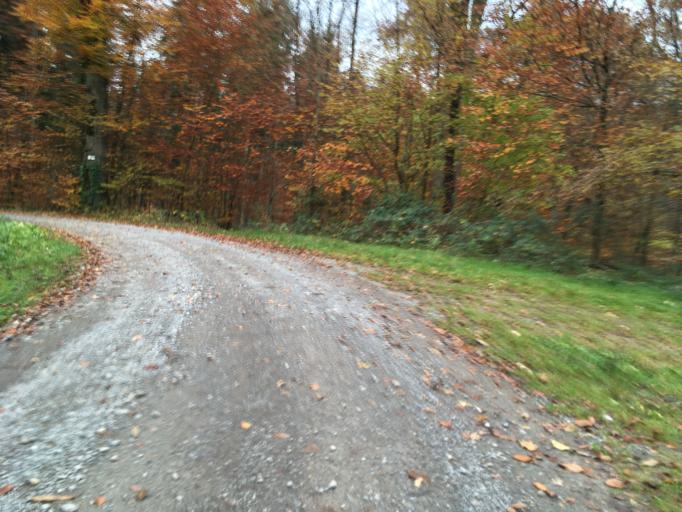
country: DE
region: Baden-Wuerttemberg
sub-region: Regierungsbezirk Stuttgart
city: Untergruppenbach
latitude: 49.0943
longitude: 9.2948
